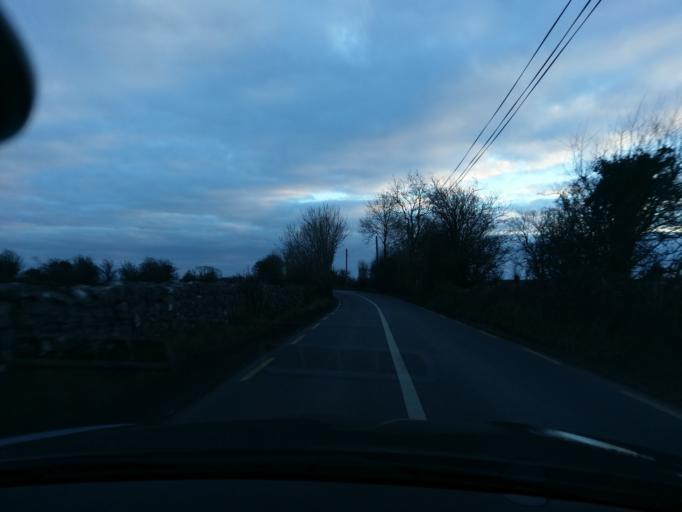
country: IE
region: Connaught
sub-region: County Galway
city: Athenry
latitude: 53.3509
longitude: -8.7777
